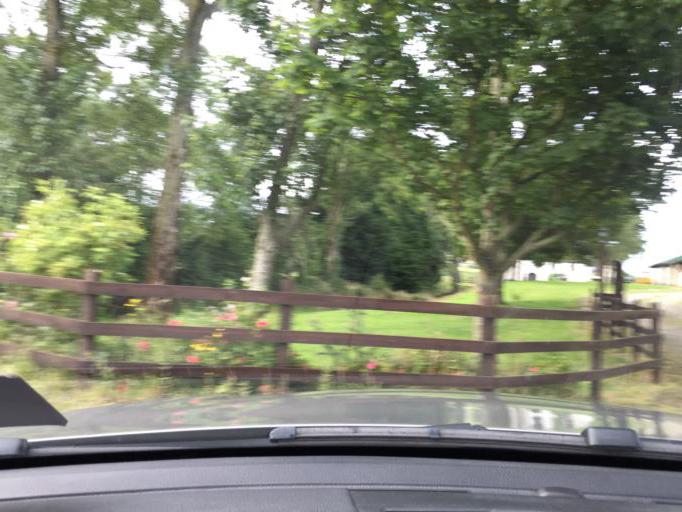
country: IE
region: Leinster
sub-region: Wicklow
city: Arklow
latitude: 52.8260
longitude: -6.1488
